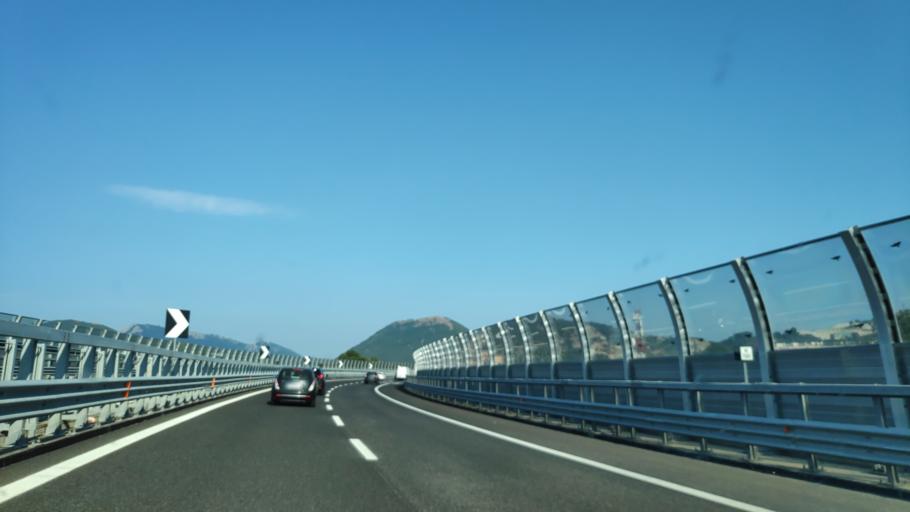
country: IT
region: Basilicate
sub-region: Provincia di Potenza
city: Lagonegro
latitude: 40.1306
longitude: 15.7646
